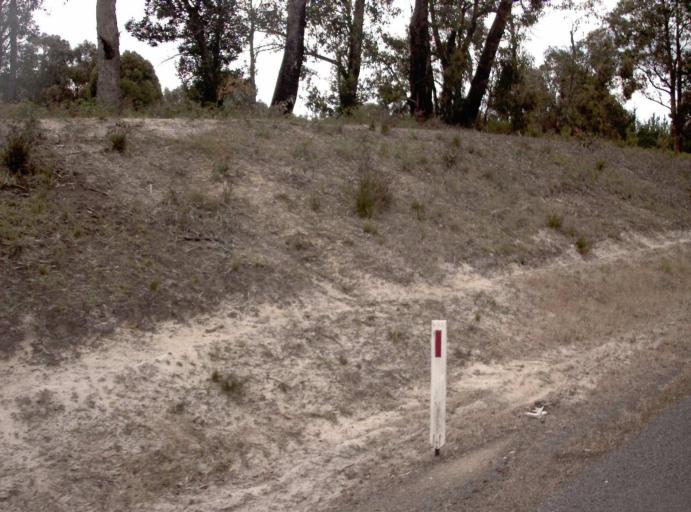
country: AU
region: Victoria
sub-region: Wellington
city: Sale
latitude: -38.3260
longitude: 147.0185
